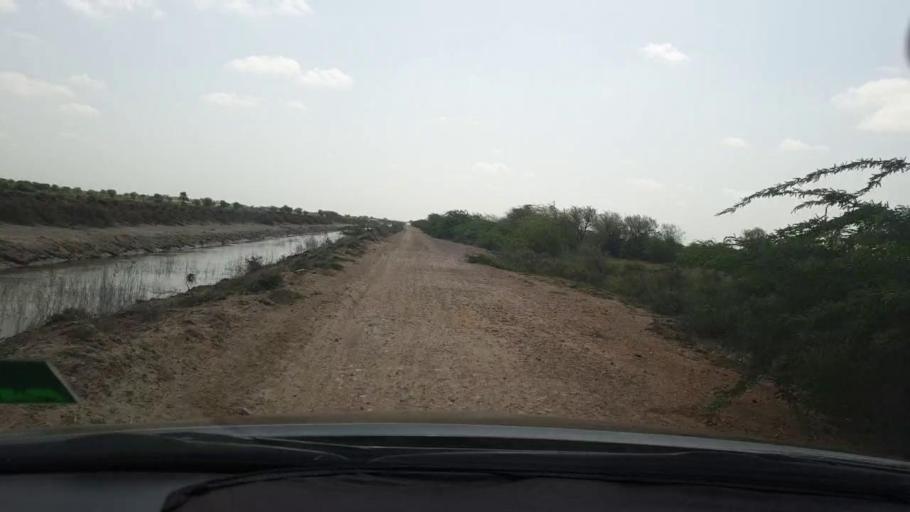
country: PK
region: Sindh
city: Tando Bago
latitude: 24.8288
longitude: 69.0612
